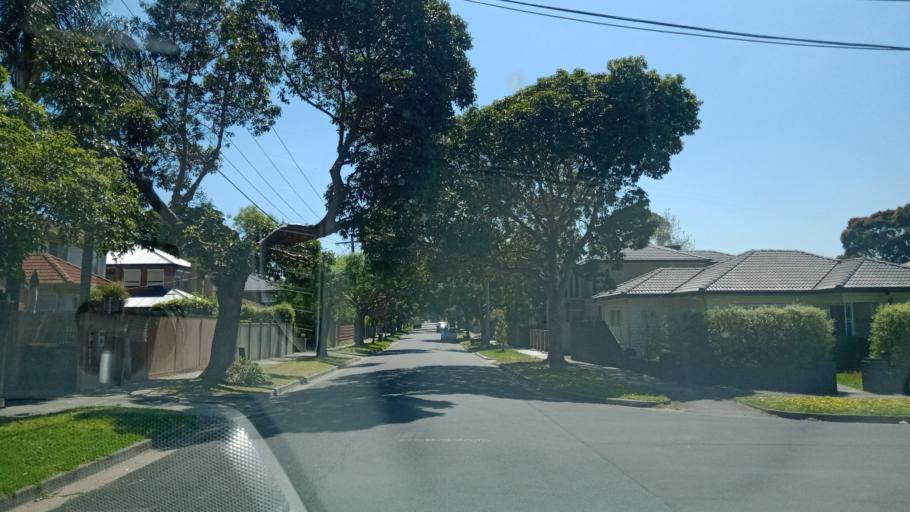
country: AU
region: Victoria
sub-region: Monash
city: Oakleigh South
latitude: -37.9302
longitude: 145.0782
